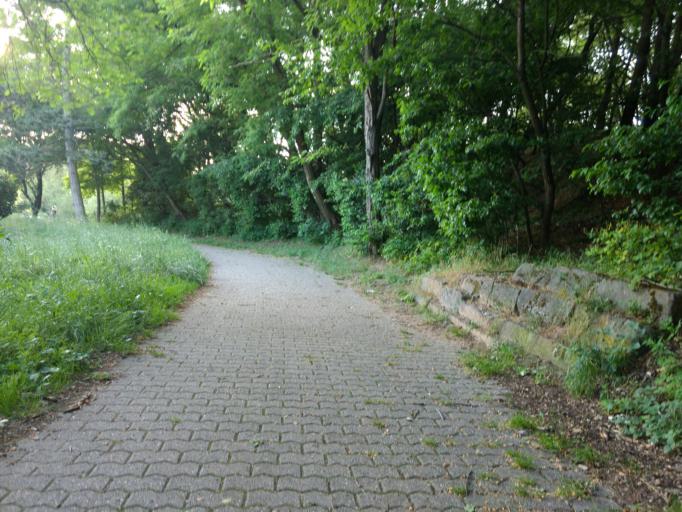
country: DE
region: Saarland
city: Saarlouis
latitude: 49.3344
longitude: 6.7618
